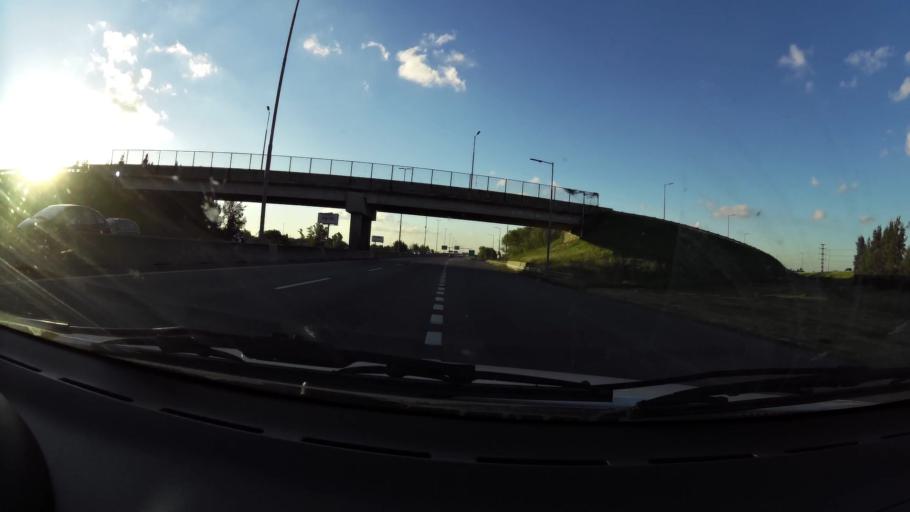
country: AR
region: Buenos Aires
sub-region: Partido de Quilmes
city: Quilmes
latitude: -34.7826
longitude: -58.1521
